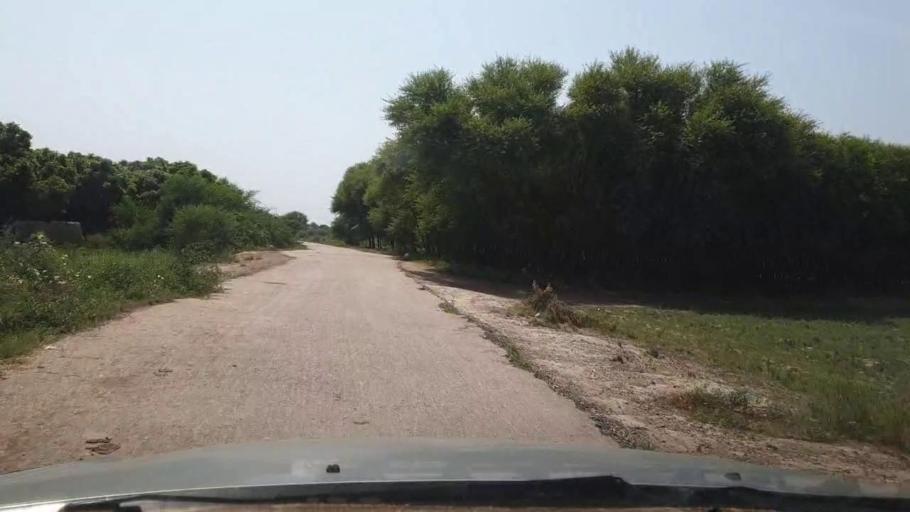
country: PK
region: Sindh
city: Chambar
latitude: 25.2298
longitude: 68.7775
